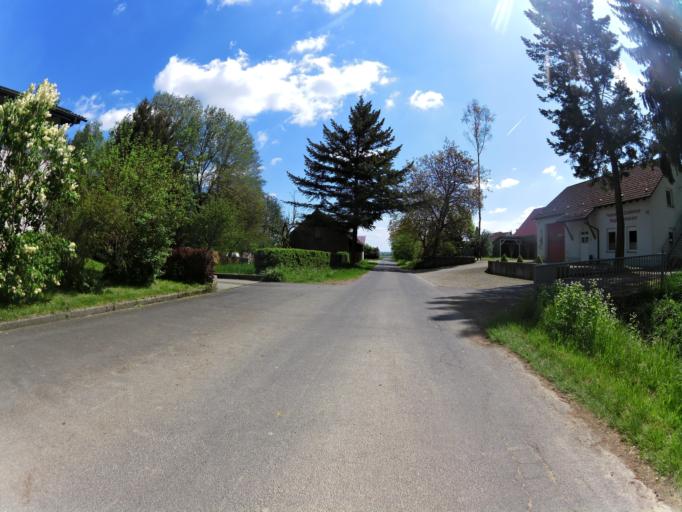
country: DE
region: Bavaria
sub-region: Regierungsbezirk Unterfranken
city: Unterpleichfeld
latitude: 49.8846
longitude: 10.0104
